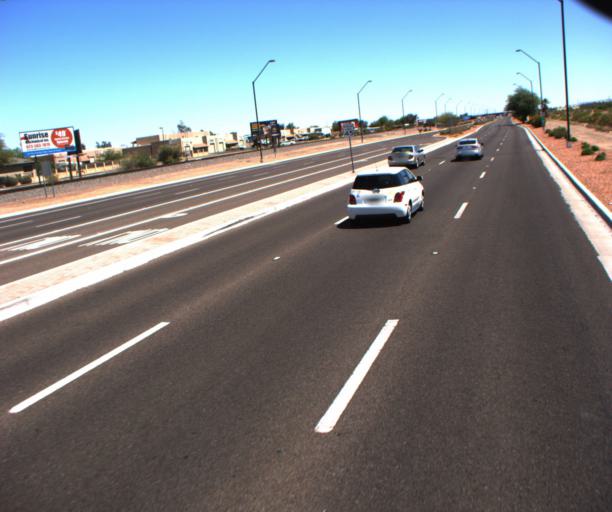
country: US
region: Arizona
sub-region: Maricopa County
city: Peoria
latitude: 33.5772
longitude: -112.2328
